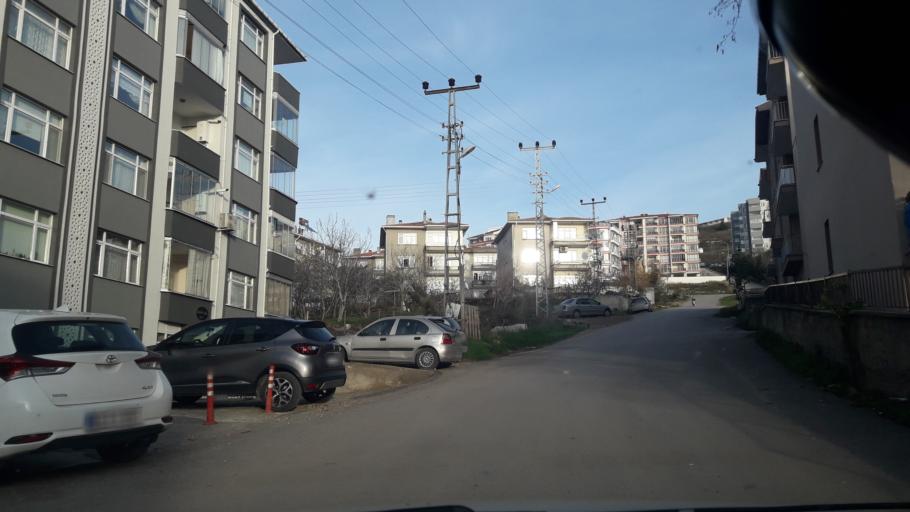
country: TR
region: Sinop
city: Sinop
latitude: 42.0288
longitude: 35.1595
